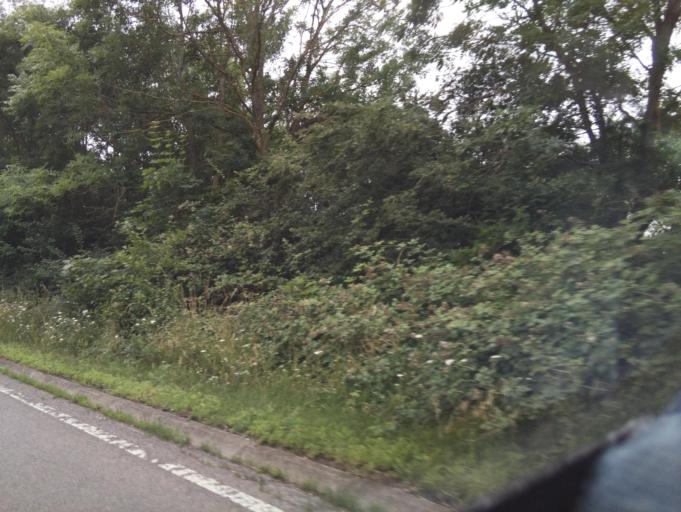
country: GB
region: England
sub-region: Northamptonshire
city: Corby
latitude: 52.4712
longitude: -0.7408
